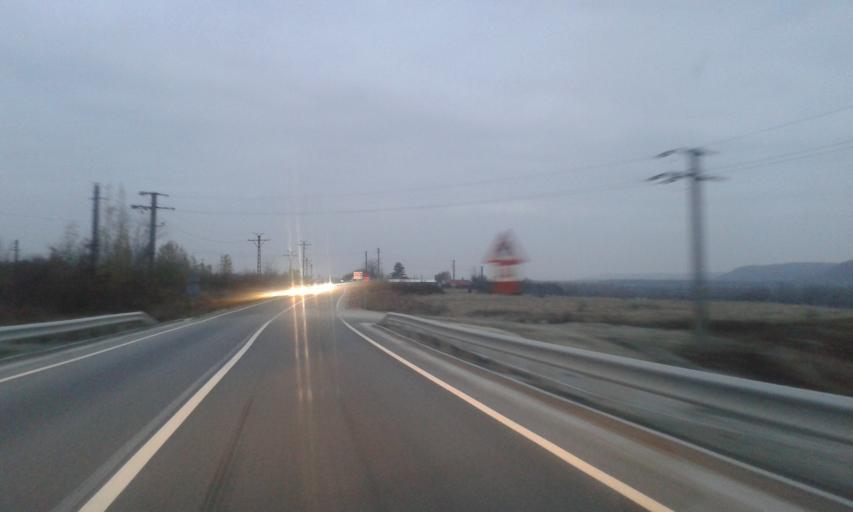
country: RO
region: Gorj
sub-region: Comuna Bumbesti-Jiu
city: Bumbesti-Jiu
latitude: 45.1593
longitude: 23.3765
